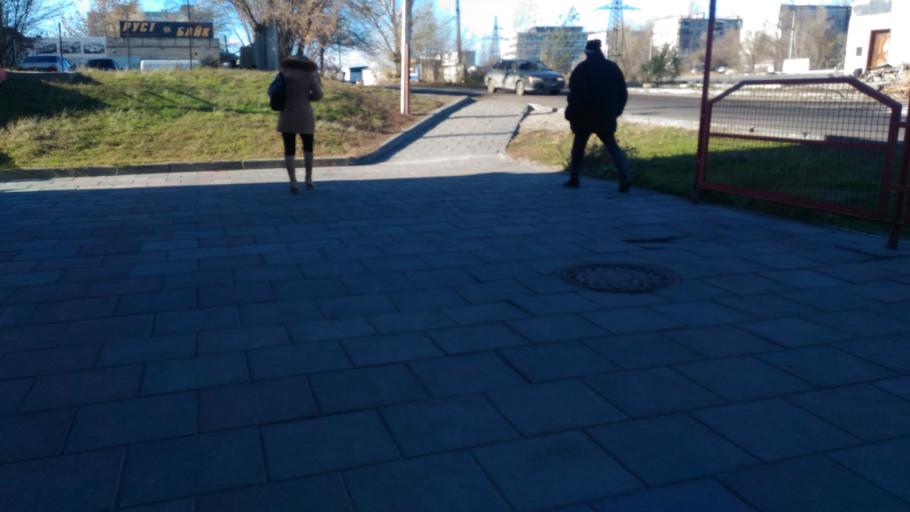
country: RU
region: Volgograd
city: Volgograd
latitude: 48.6543
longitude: 44.4412
